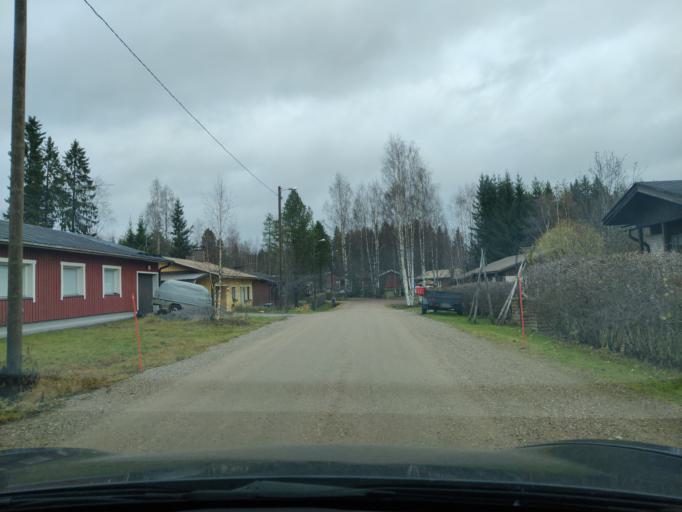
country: FI
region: Northern Savo
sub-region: Ylae-Savo
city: Kiuruvesi
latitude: 63.6434
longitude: 26.6411
